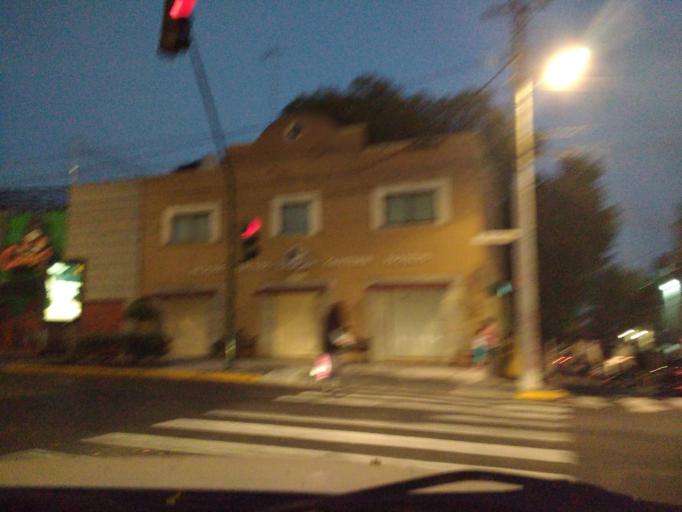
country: MX
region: Mexico City
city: Tlalpan
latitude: 19.2868
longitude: -99.1635
